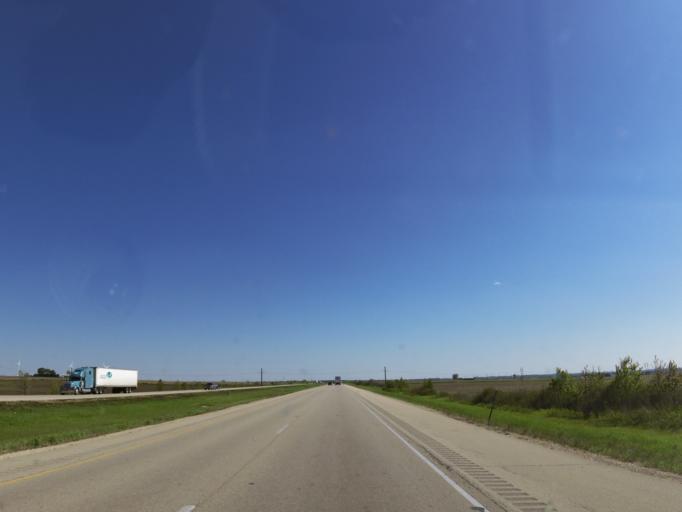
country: US
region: Illinois
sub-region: Ogle County
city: Rochelle
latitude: 41.8312
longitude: -89.0101
